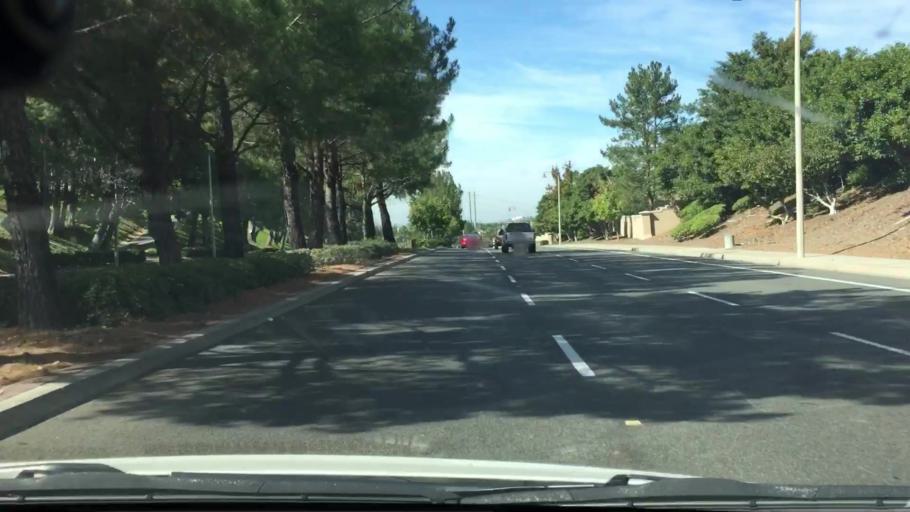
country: US
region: California
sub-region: Orange County
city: Rancho Santa Margarita
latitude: 33.6484
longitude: -117.6290
